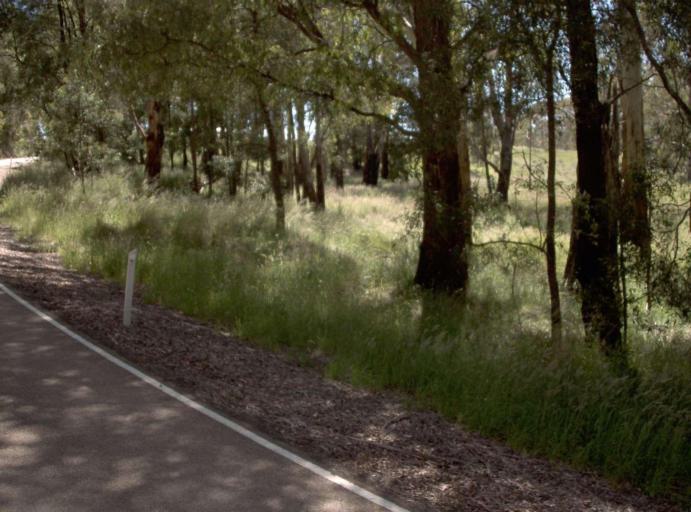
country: AU
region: Victoria
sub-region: East Gippsland
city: Lakes Entrance
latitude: -37.2232
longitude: 148.2634
